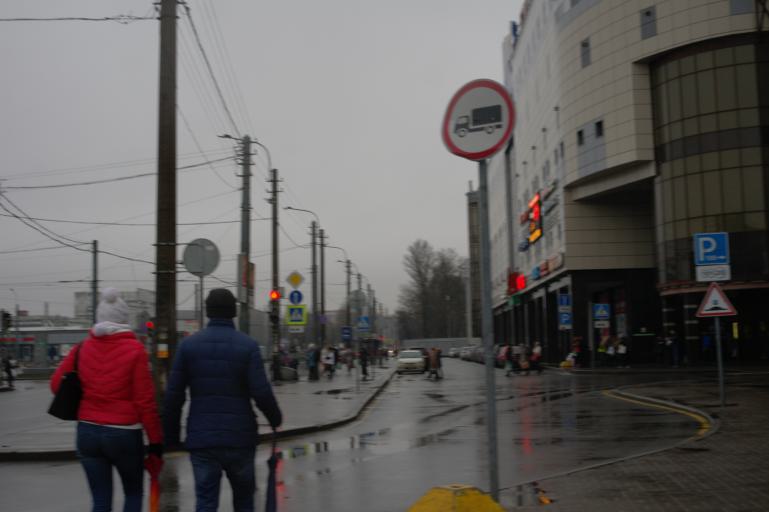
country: RU
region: St.-Petersburg
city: Staraya Derevnya
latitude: 59.9893
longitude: 30.2563
